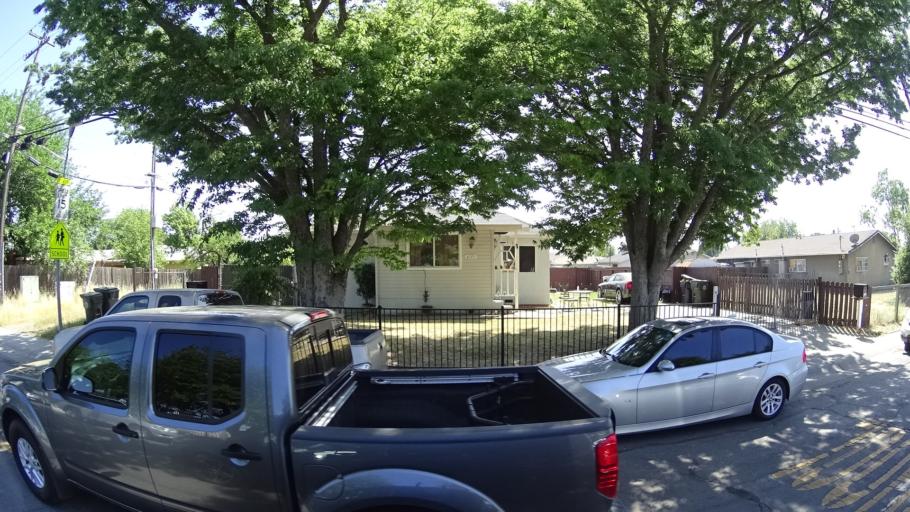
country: US
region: California
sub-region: Sacramento County
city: Parkway
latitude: 38.5038
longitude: -121.4788
